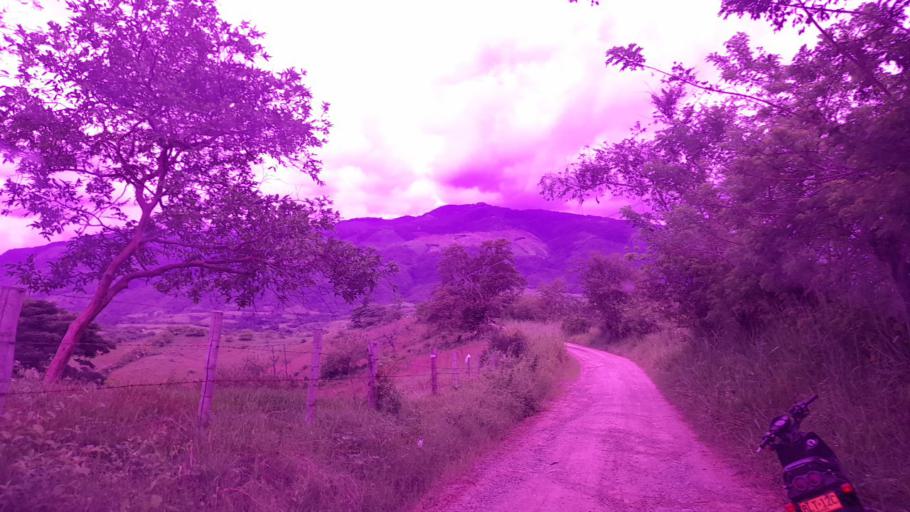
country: CO
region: Valle del Cauca
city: Andalucia
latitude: 4.1725
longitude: -76.0964
